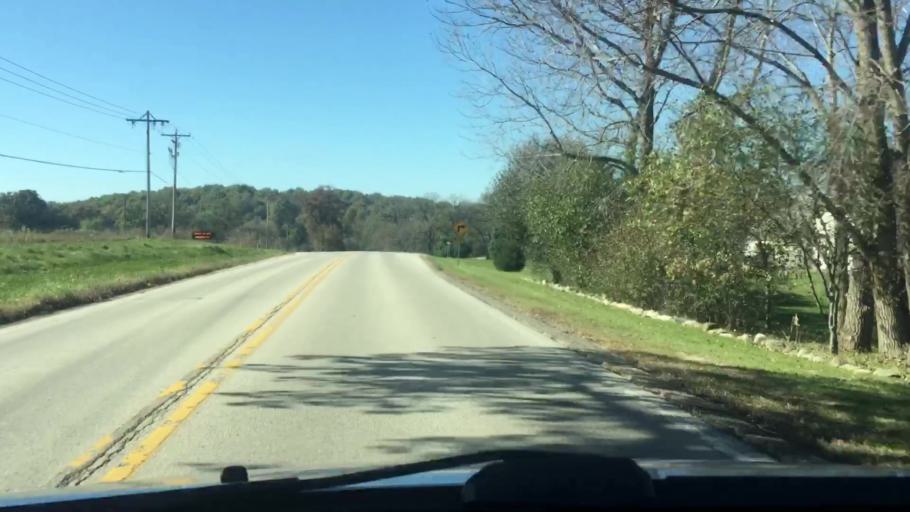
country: US
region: Wisconsin
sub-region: Waukesha County
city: Wales
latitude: 42.9882
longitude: -88.3572
